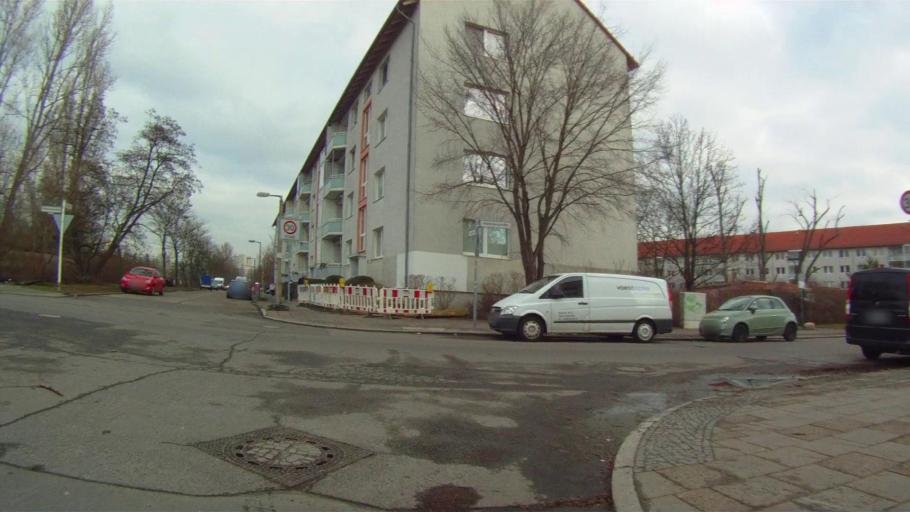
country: DE
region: Berlin
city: Karlshorst
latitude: 52.4880
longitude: 13.5160
